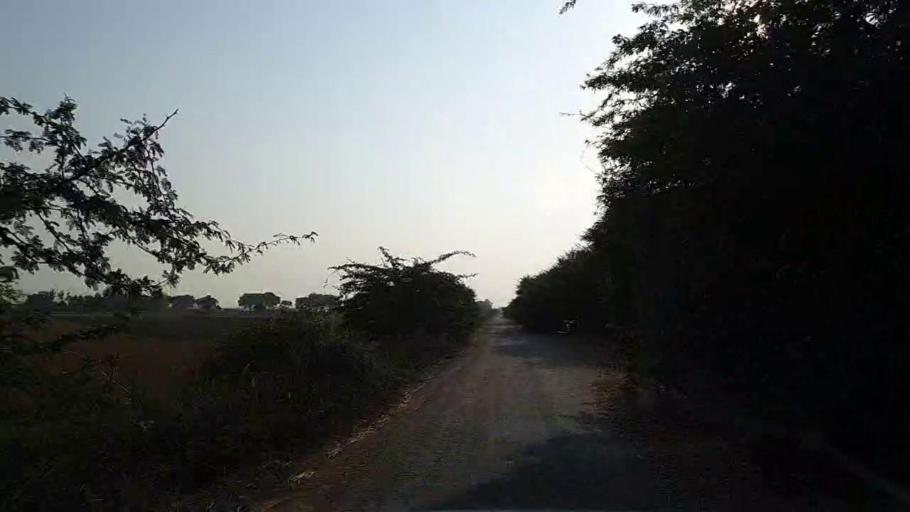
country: PK
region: Sindh
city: Mirpur Batoro
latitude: 24.7800
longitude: 68.2427
